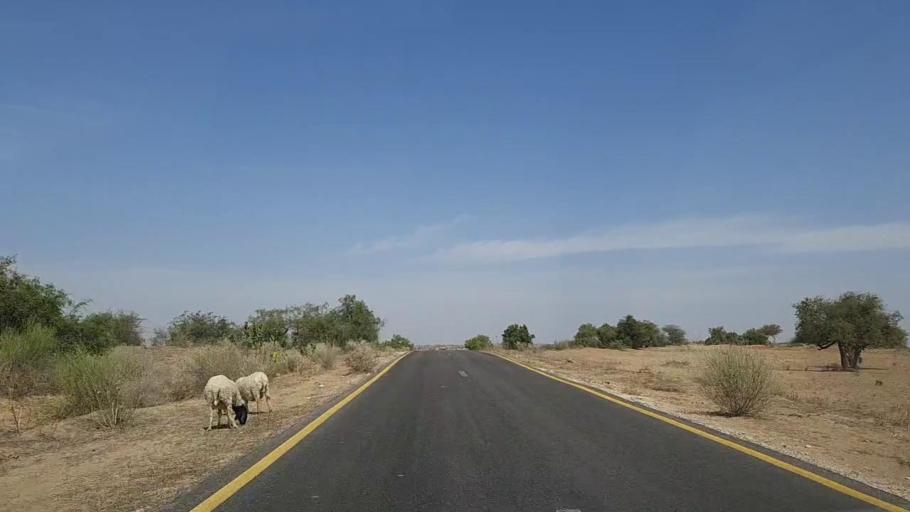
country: PK
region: Sindh
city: Mithi
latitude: 24.9137
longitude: 69.8910
